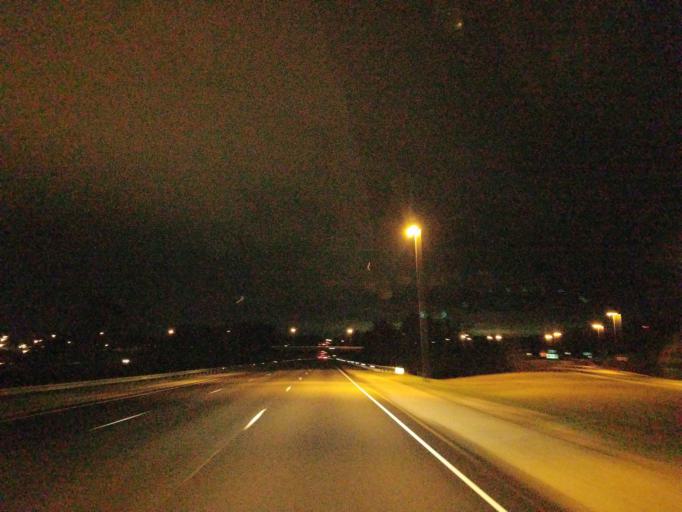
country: US
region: Alabama
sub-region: Tuscaloosa County
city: Vance
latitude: 33.1943
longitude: -87.2461
